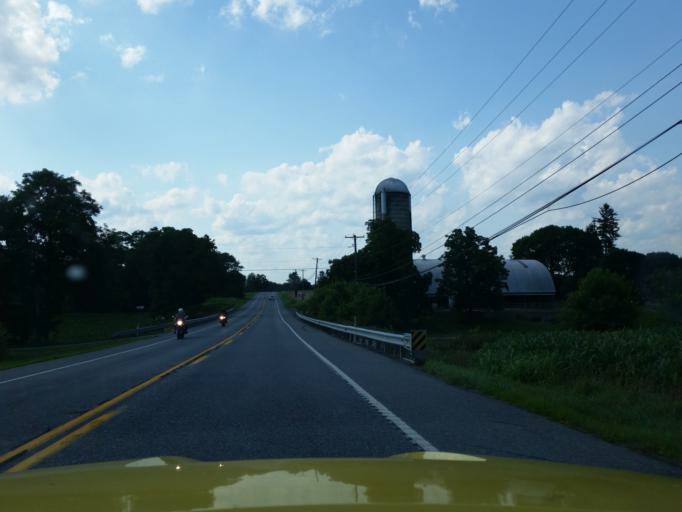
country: US
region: Pennsylvania
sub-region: Lebanon County
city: Annville
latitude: 40.3056
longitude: -76.4979
